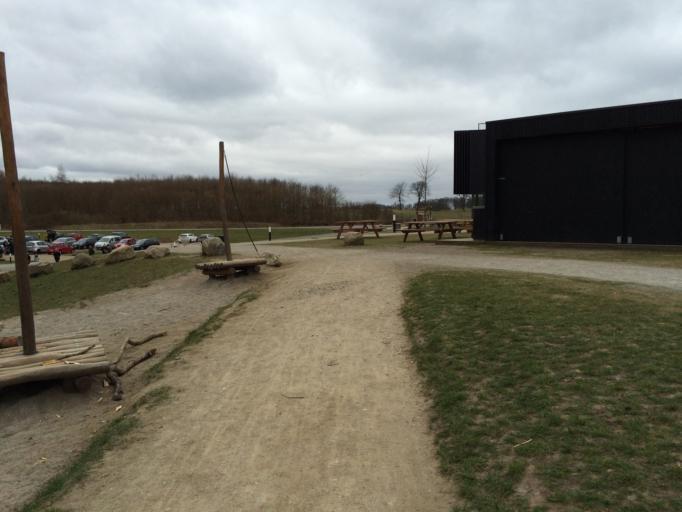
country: DK
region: South Denmark
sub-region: Fredericia Kommune
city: Snoghoj
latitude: 55.5118
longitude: 9.7010
